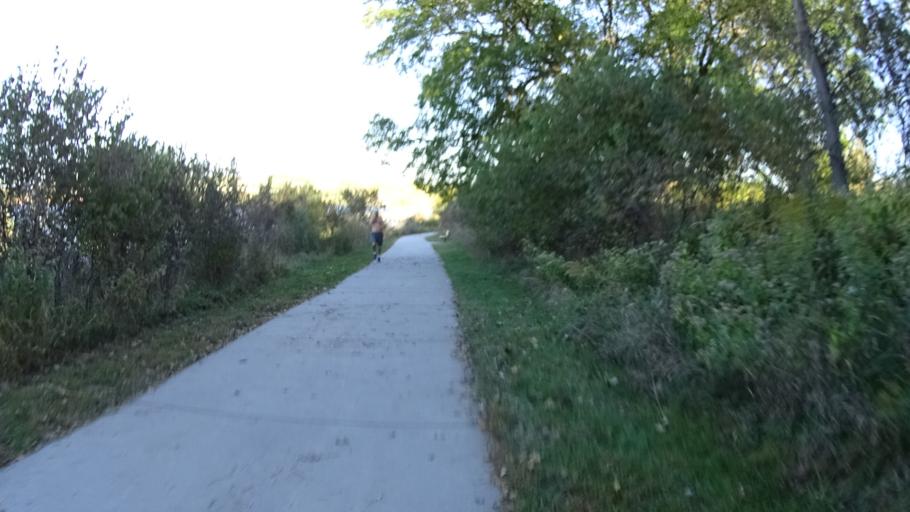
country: US
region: Nebraska
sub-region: Sarpy County
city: Papillion
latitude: 41.1399
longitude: -96.0711
